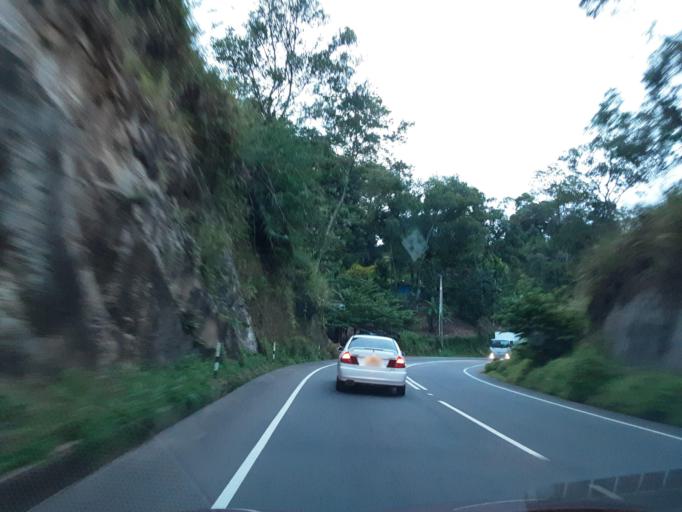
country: LK
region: Uva
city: Badulla
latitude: 6.9122
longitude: 80.9336
